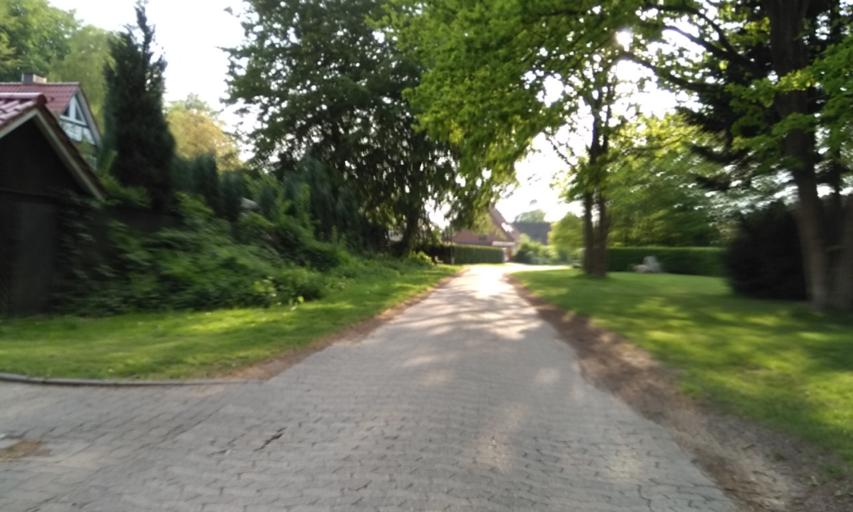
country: DE
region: Lower Saxony
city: Nottensdorf
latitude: 53.4849
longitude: 9.6079
